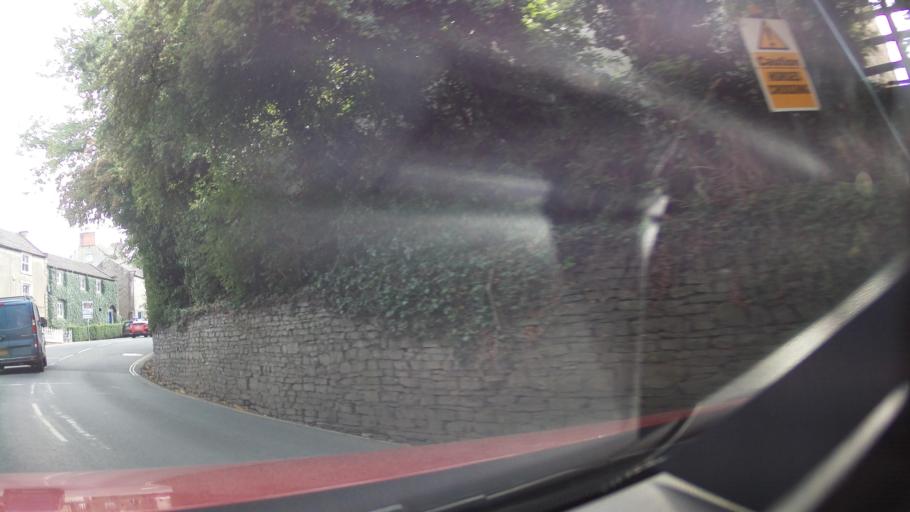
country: GB
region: England
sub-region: North Yorkshire
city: Leyburn
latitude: 54.2870
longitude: -1.8062
